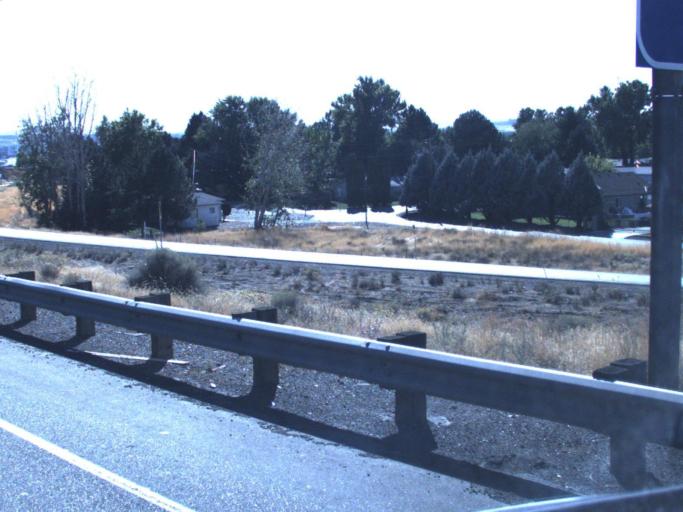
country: US
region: Washington
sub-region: Franklin County
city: Pasco
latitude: 46.2478
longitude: -119.1265
